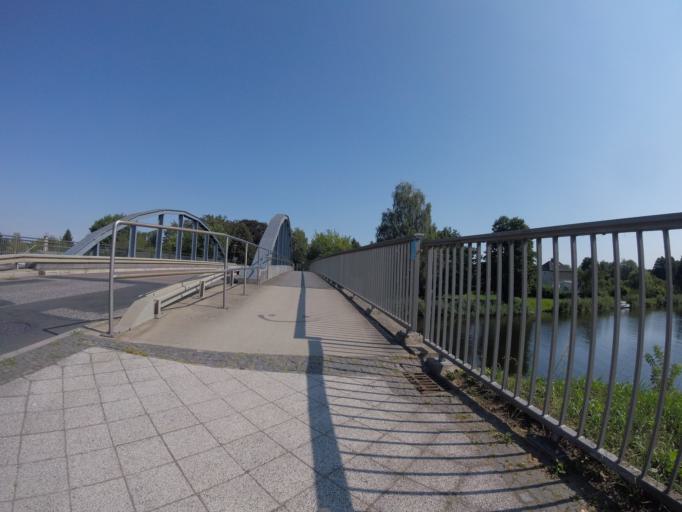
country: DE
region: Brandenburg
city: Mullrose
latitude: 52.2516
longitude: 14.4206
